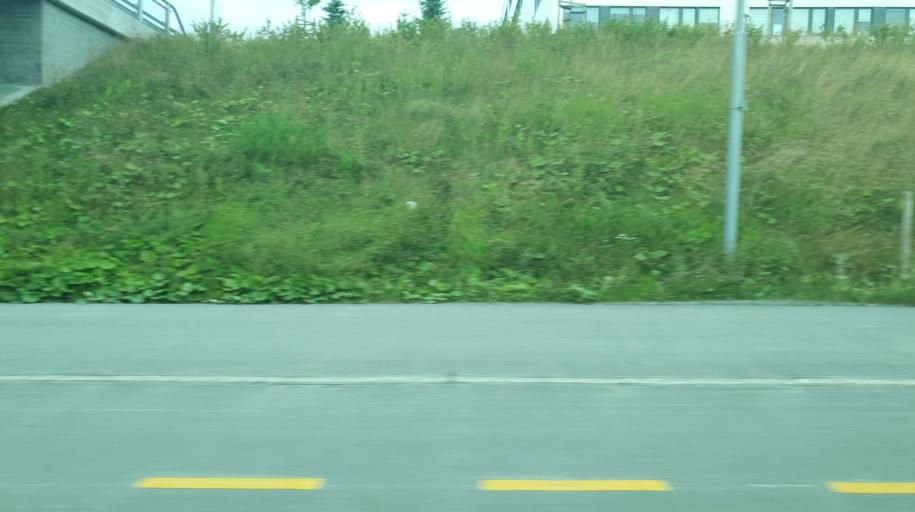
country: NO
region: Sor-Trondelag
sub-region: Trondheim
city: Trondheim
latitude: 63.3607
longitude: 10.3699
